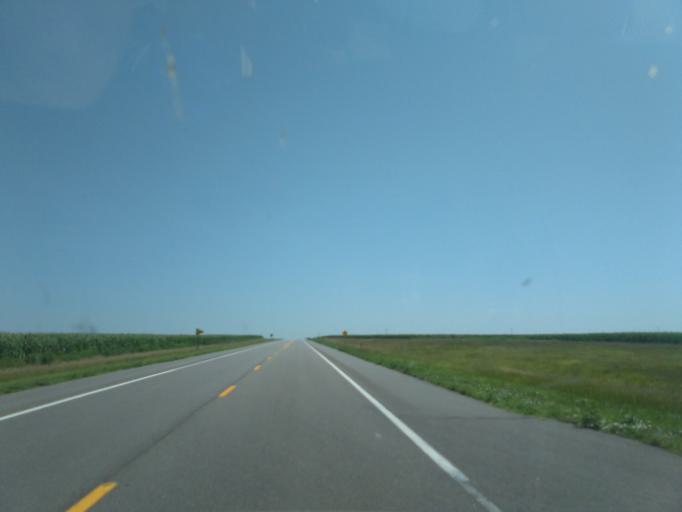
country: US
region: Nebraska
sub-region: Hitchcock County
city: Trenton
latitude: 40.2079
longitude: -100.9625
